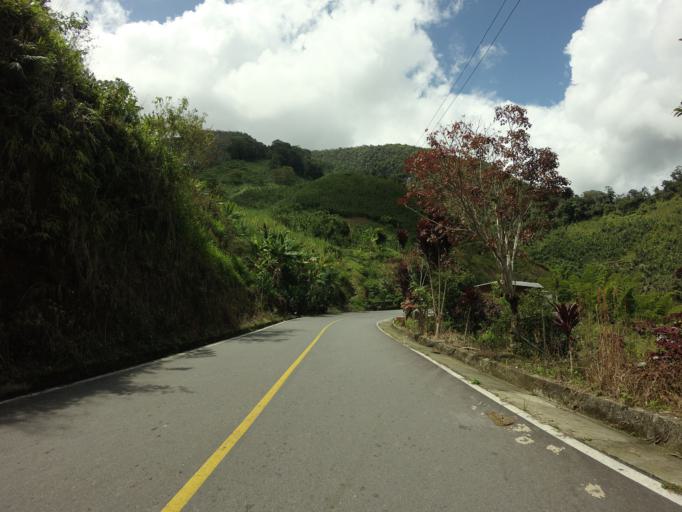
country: CO
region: Caldas
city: Marquetalia
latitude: 5.2868
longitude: -75.1053
